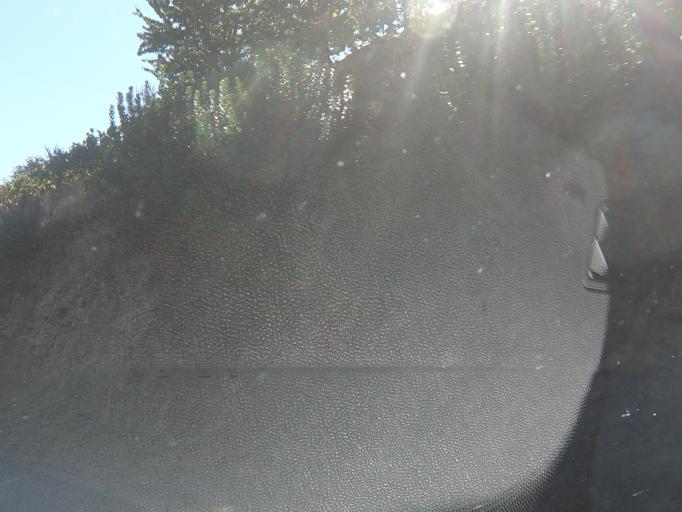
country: PT
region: Vila Real
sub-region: Santa Marta de Penaguiao
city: Santa Marta de Penaguiao
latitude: 41.2348
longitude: -7.7921
